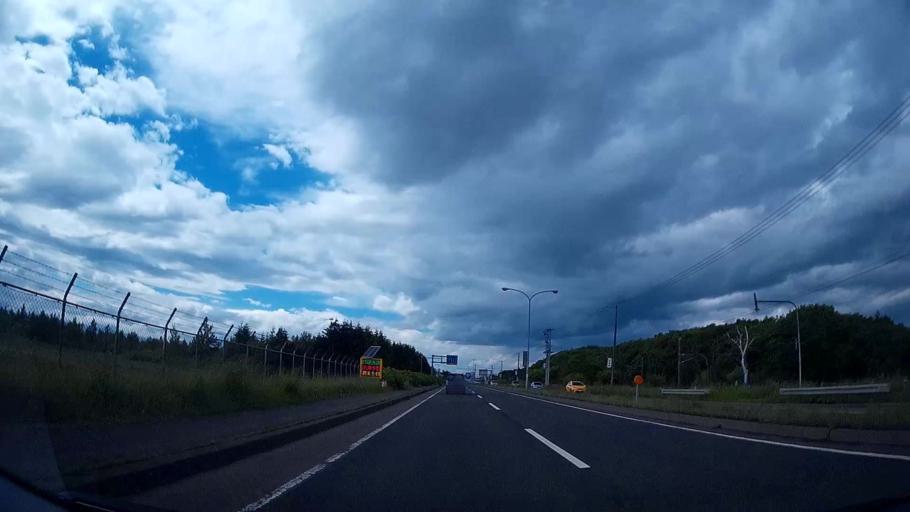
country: JP
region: Hokkaido
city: Chitose
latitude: 42.8155
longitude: 141.6660
